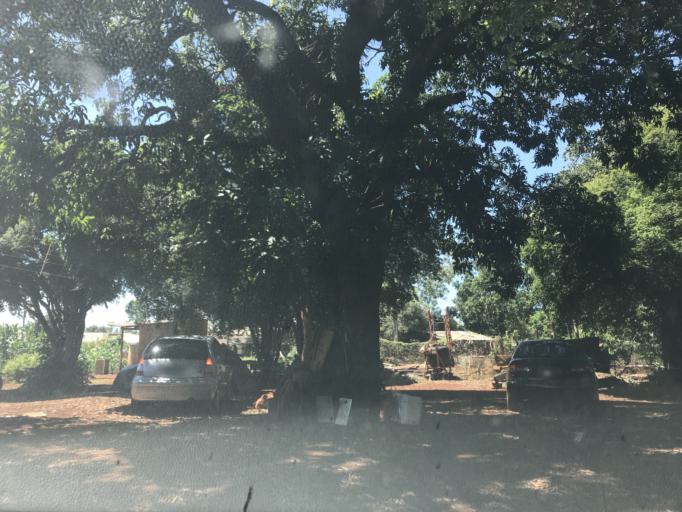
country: BR
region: Parana
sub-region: Londrina
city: Londrina
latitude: -23.3492
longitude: -51.1618
